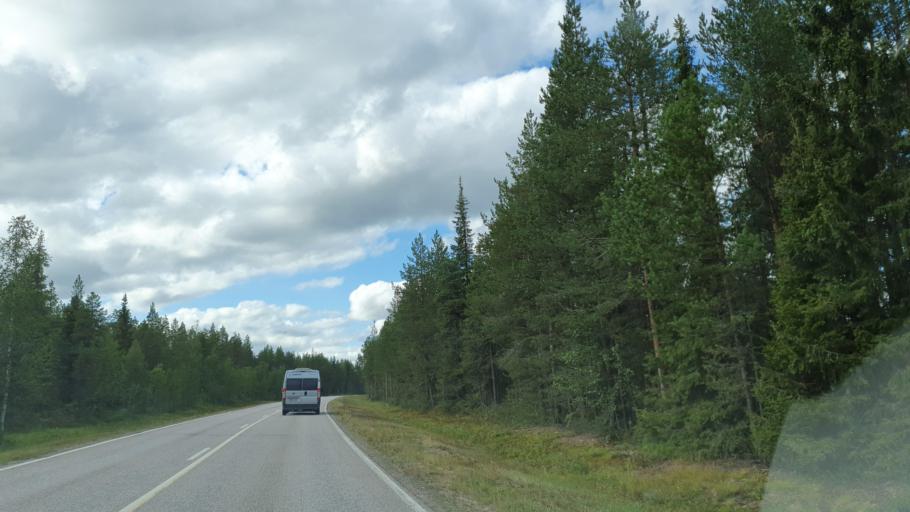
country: FI
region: Lapland
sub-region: Tunturi-Lappi
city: Muonio
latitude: 67.8599
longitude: 24.1409
